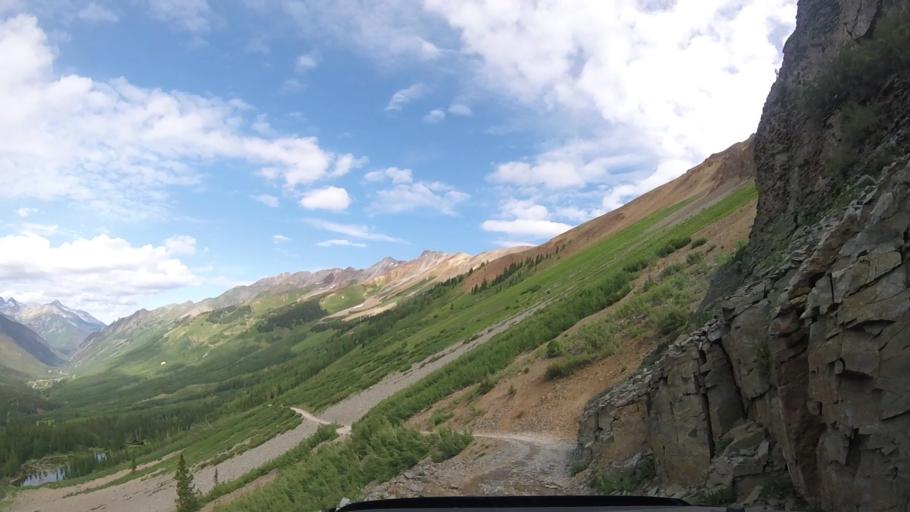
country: US
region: Colorado
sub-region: San Miguel County
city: Telluride
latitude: 37.8562
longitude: -107.7875
